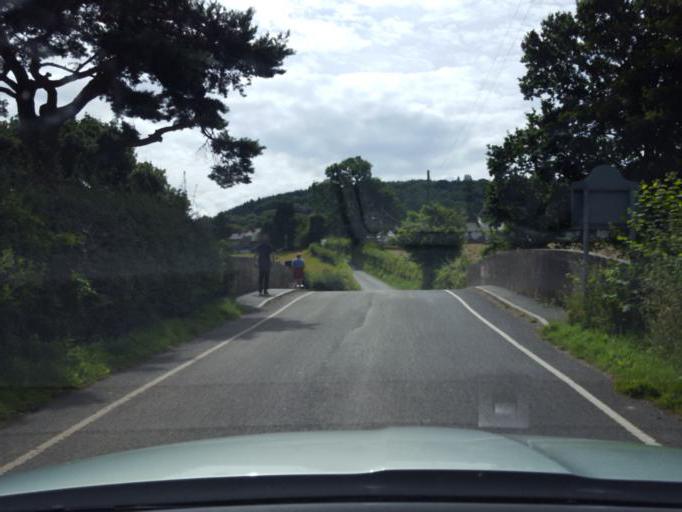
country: GB
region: Wales
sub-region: Denbighshire
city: Bryneglwys
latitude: 52.9818
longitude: -3.3160
